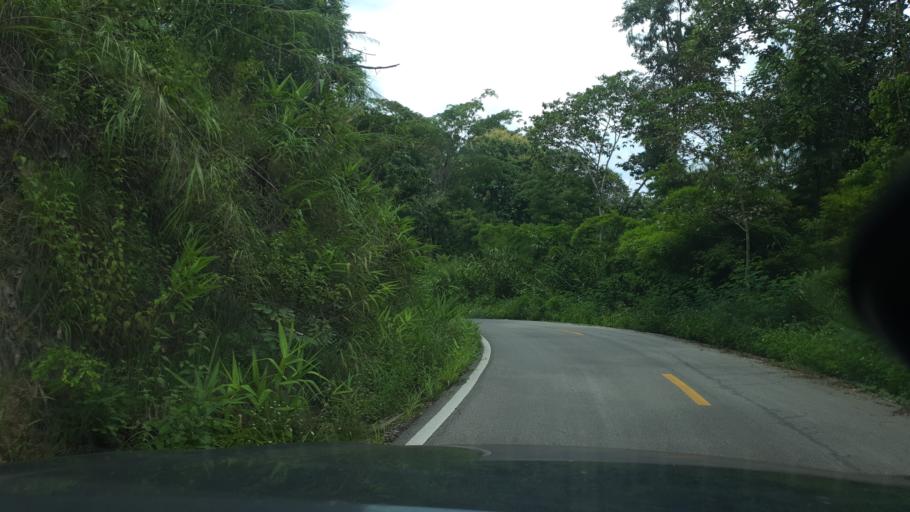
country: TH
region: Lamphun
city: Mae Tha
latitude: 18.5098
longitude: 99.2631
